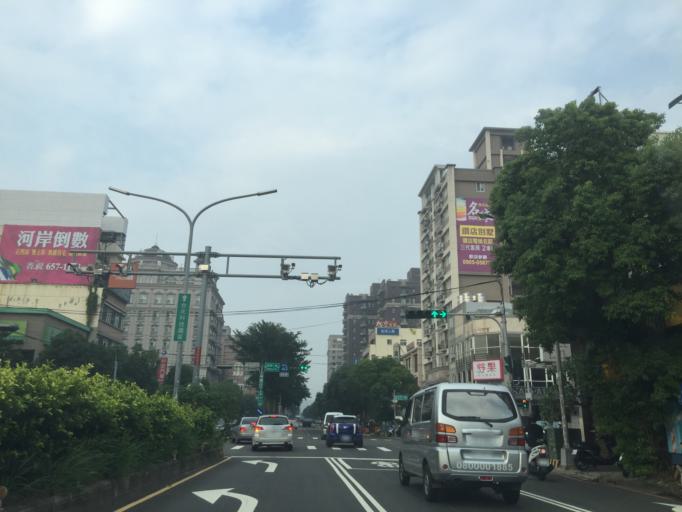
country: TW
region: Taiwan
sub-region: Hsinchu
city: Zhubei
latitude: 24.8297
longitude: 121.0174
